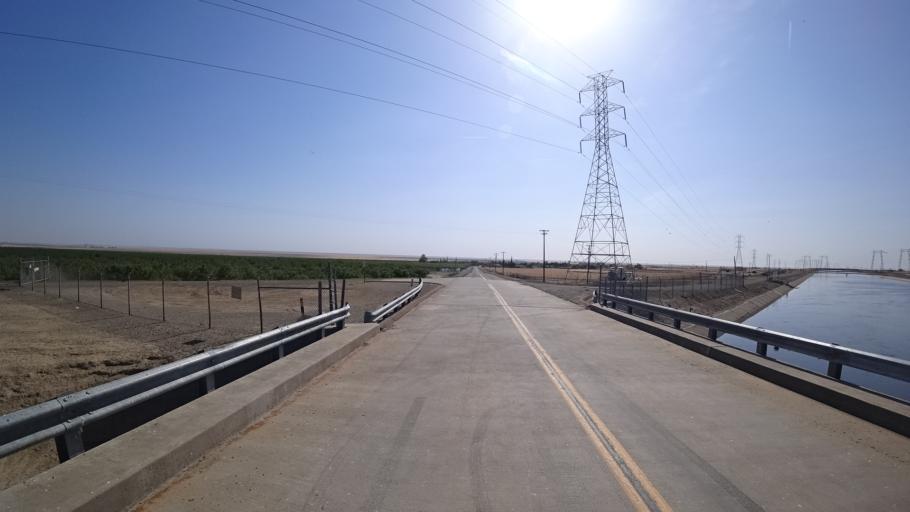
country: US
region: California
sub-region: Kings County
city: Kettleman City
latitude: 36.0100
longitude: -119.9743
